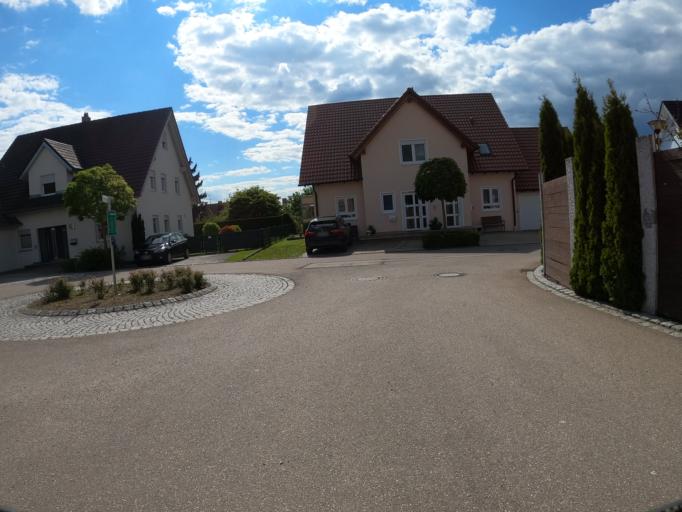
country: DE
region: Bavaria
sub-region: Swabia
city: Bubesheim
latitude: 48.4347
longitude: 10.2598
